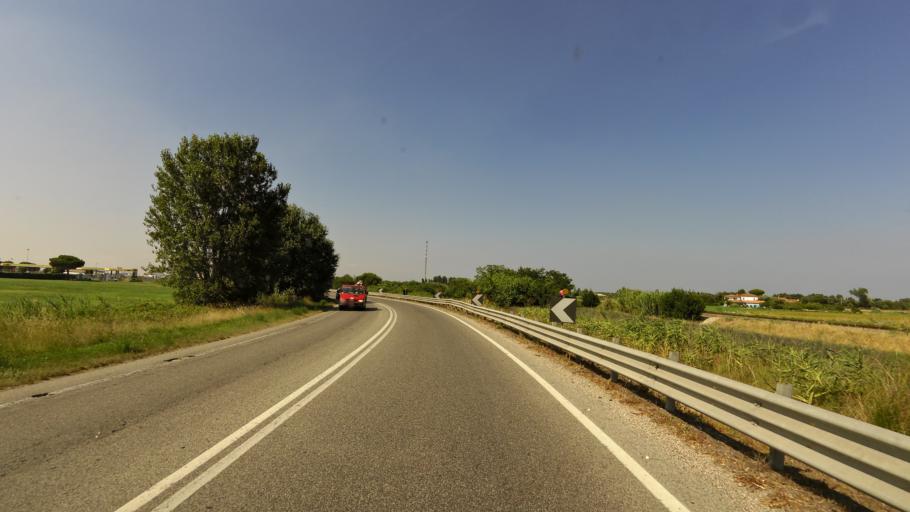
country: IT
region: Emilia-Romagna
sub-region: Provincia di Ravenna
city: Porto Fuori
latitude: 44.4137
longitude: 12.2341
